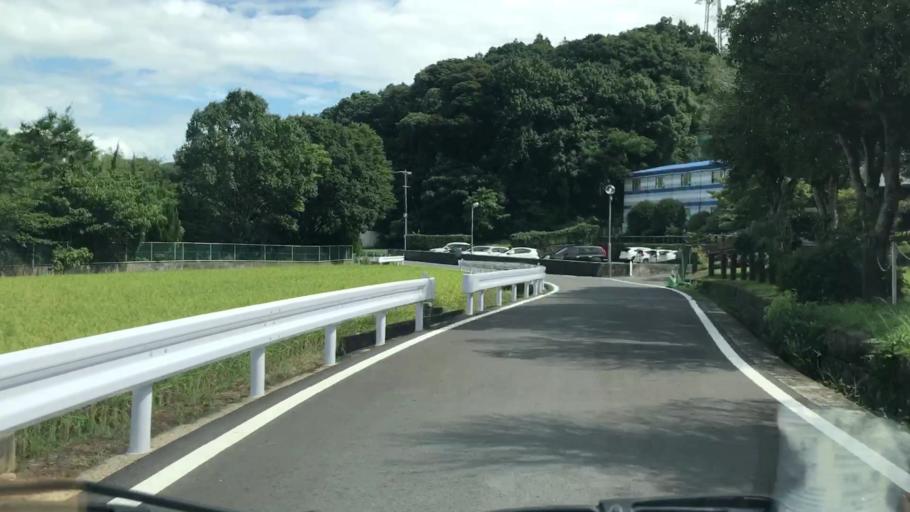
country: JP
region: Saga Prefecture
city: Saga-shi
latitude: 33.2307
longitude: 130.1755
